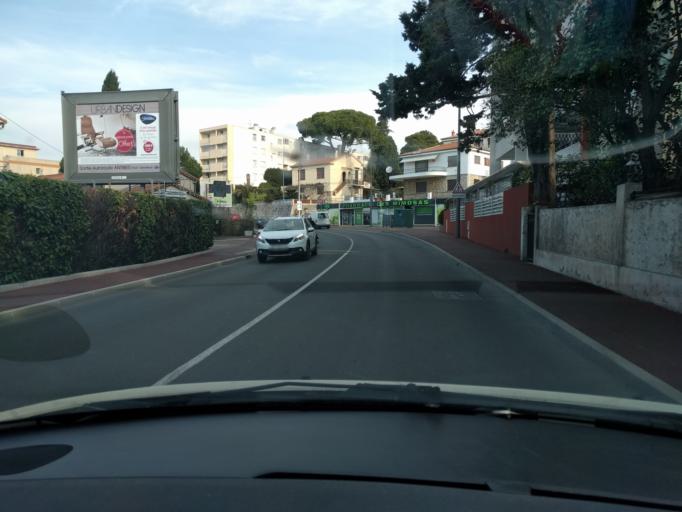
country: FR
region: Provence-Alpes-Cote d'Azur
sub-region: Departement des Alpes-Maritimes
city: Mandelieu-la-Napoule
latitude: 43.5551
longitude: 6.9720
